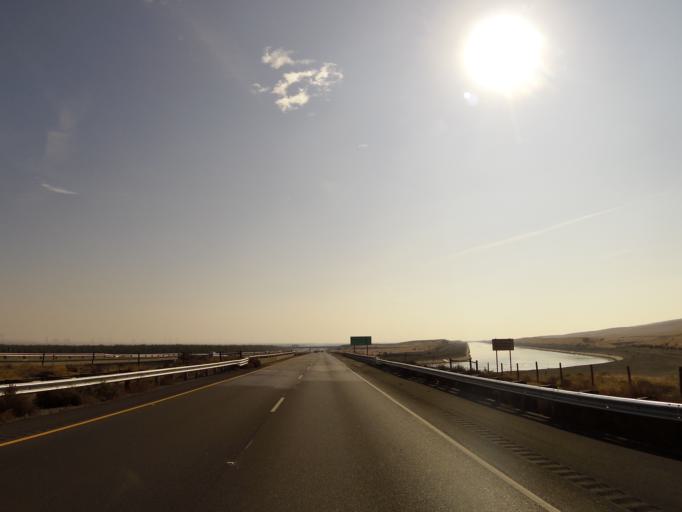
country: US
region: California
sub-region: Kings County
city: Kettleman City
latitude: 35.9637
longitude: -119.9422
